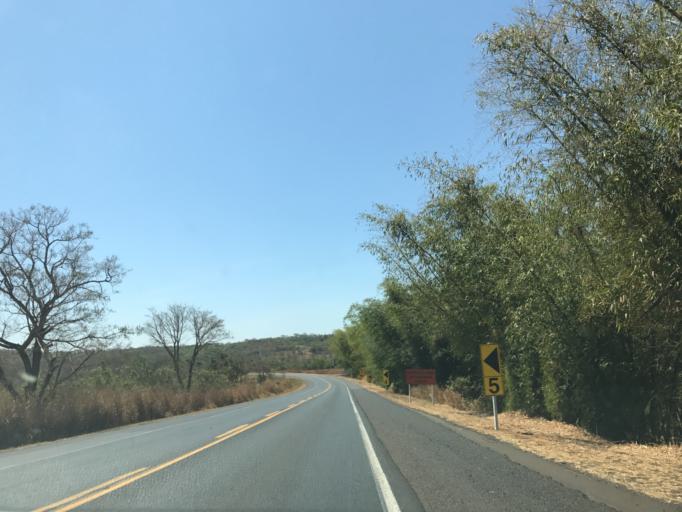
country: BR
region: Minas Gerais
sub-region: Prata
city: Prata
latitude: -19.3532
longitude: -48.8979
